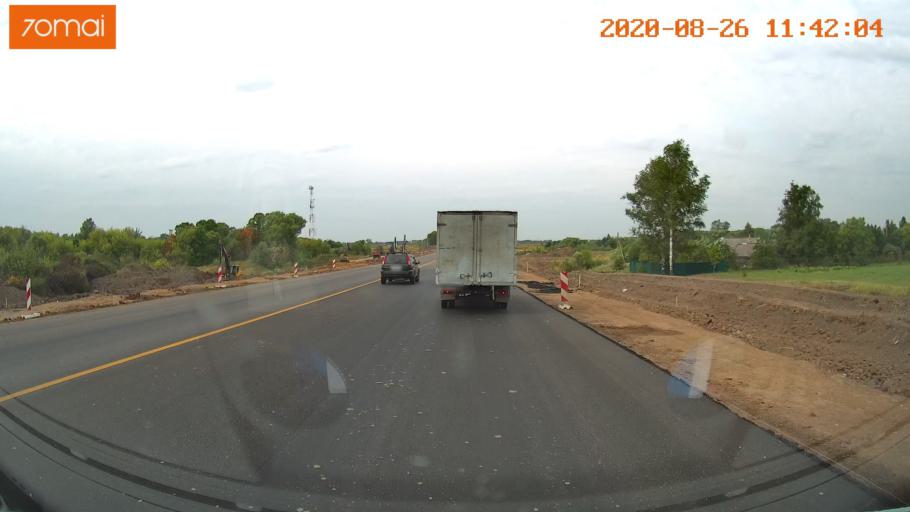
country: RU
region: Rjazan
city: Shilovo
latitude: 54.2962
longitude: 40.6999
